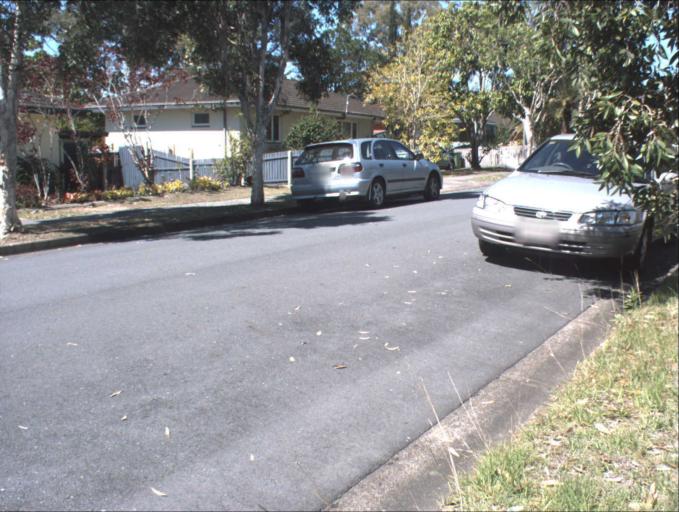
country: AU
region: Queensland
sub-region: Logan
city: Logan City
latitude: -27.6375
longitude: 153.1098
